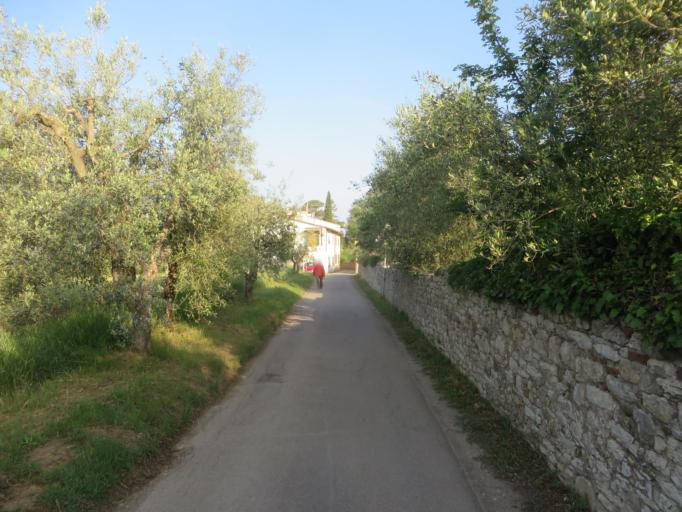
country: IT
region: Tuscany
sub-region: Province of Florence
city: Bagno a Ripoli
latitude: 43.7475
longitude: 11.3238
